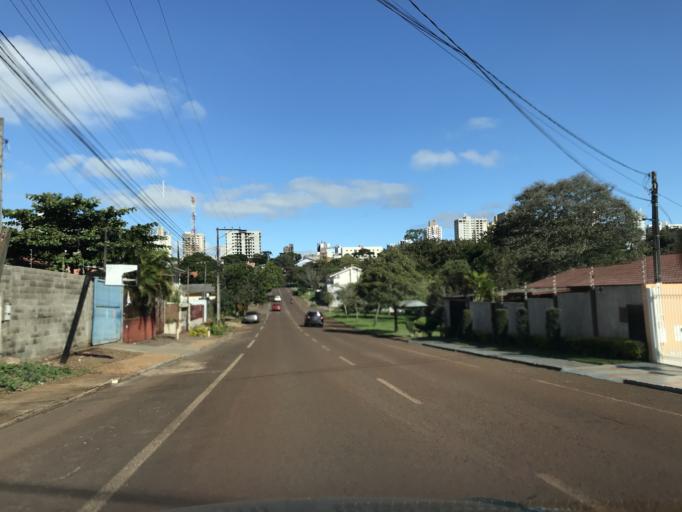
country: BR
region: Parana
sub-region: Cascavel
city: Cascavel
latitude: -24.9456
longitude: -53.4687
